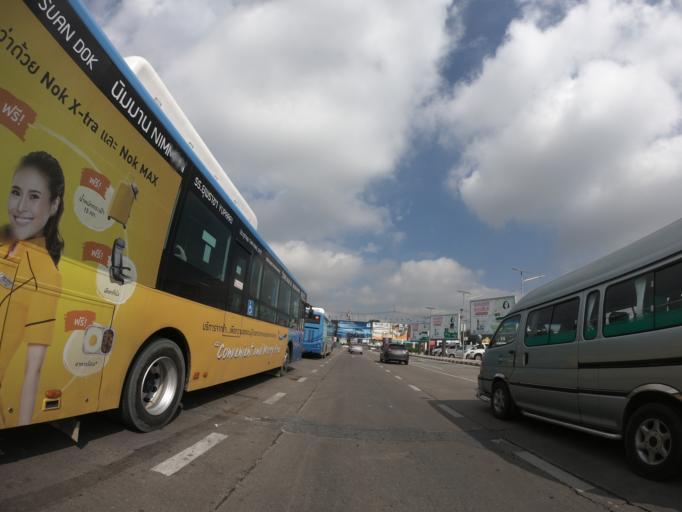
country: TH
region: Chiang Mai
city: Chiang Mai
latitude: 18.7711
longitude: 98.9680
